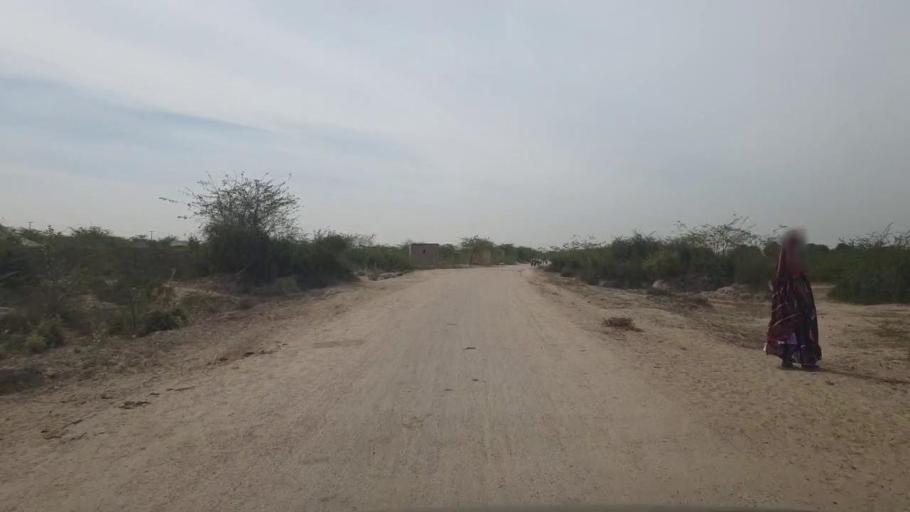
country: PK
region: Sindh
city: Umarkot
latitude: 25.2531
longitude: 69.7214
